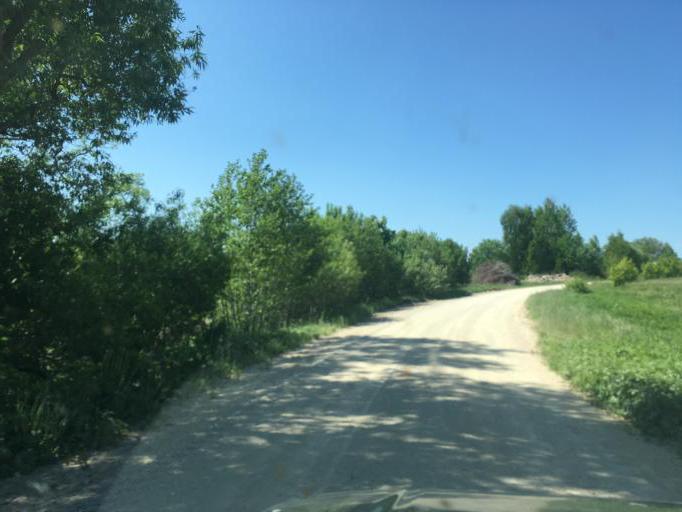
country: LV
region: Talsu Rajons
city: Valdemarpils
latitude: 57.4269
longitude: 22.6785
